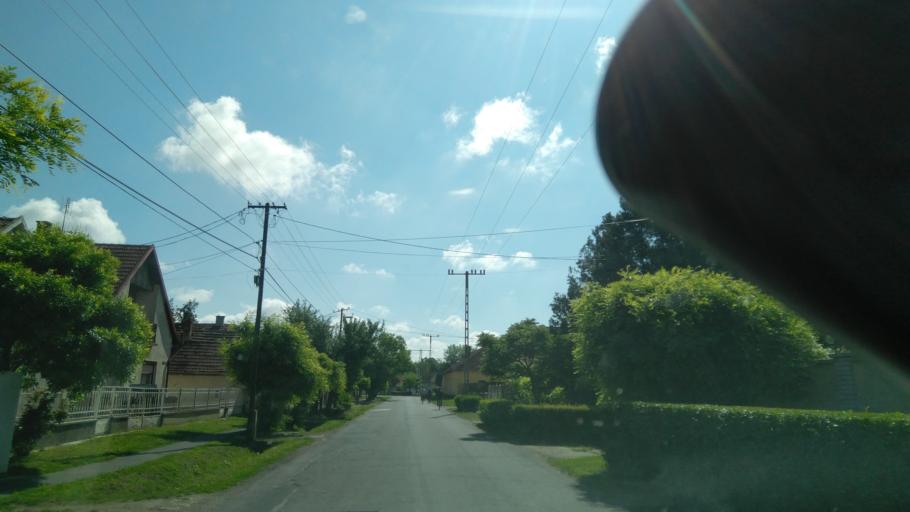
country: HU
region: Bekes
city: Bekes
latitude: 46.7761
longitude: 21.1244
